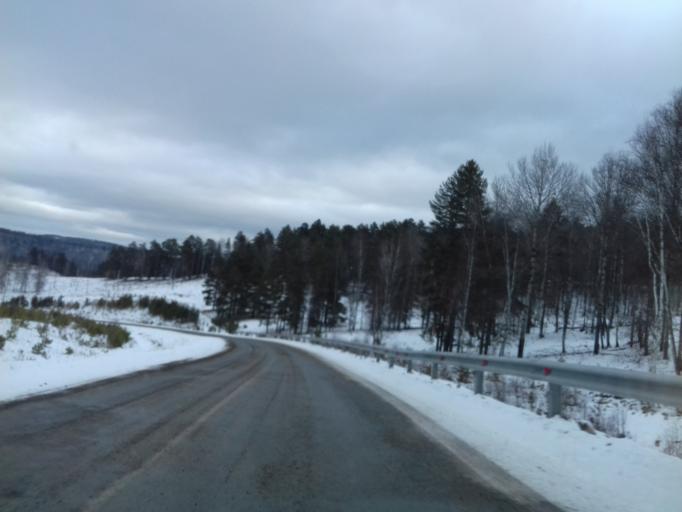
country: RU
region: Bashkortostan
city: Starosubkhangulovo
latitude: 53.2767
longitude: 57.5262
